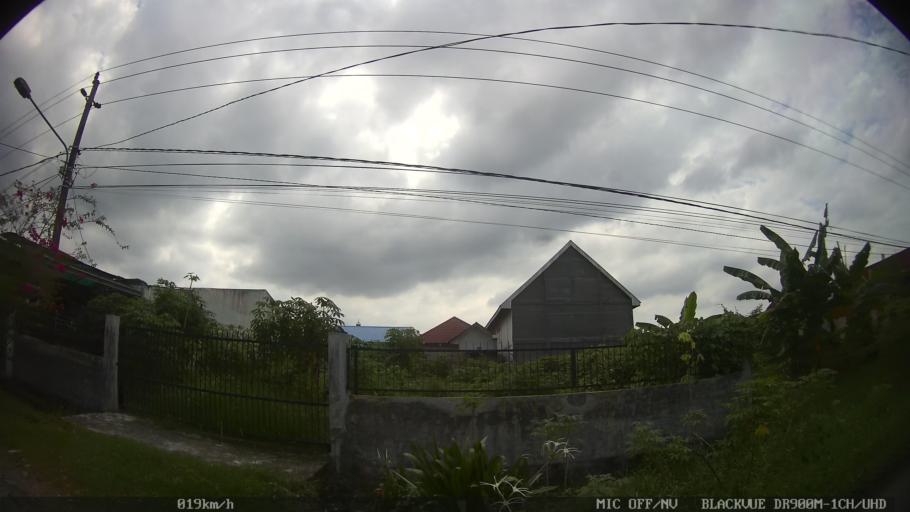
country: ID
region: North Sumatra
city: Sunggal
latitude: 3.6108
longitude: 98.6236
